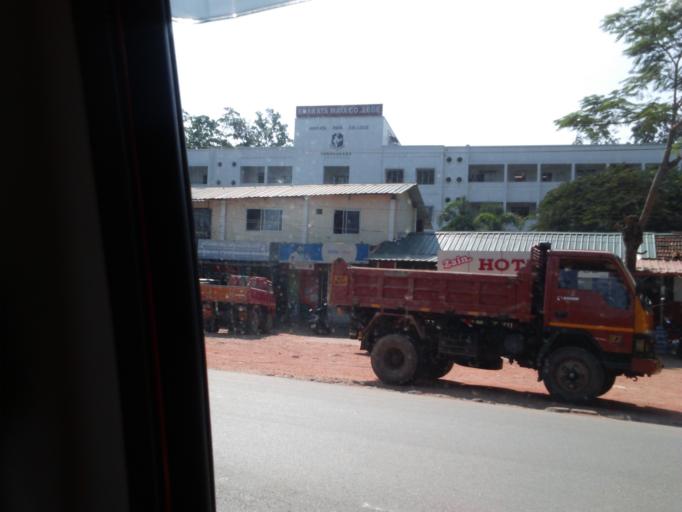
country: IN
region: Kerala
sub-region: Ernakulam
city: Elur
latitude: 10.0302
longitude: 76.3363
